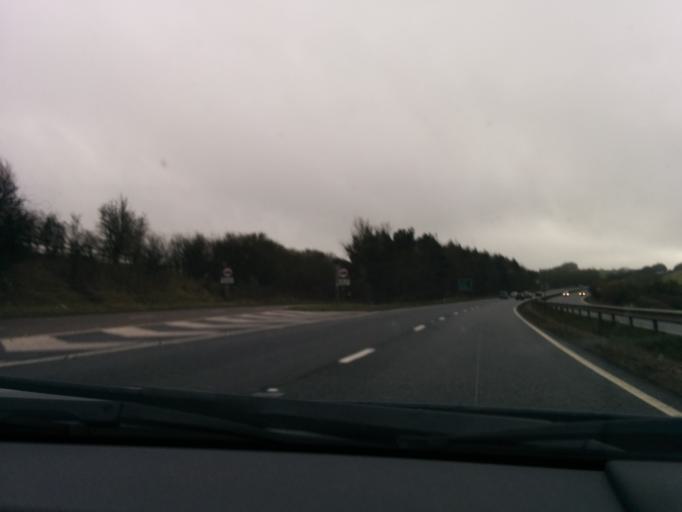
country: GB
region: England
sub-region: West Berkshire
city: Hermitage
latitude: 51.5009
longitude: -1.2929
